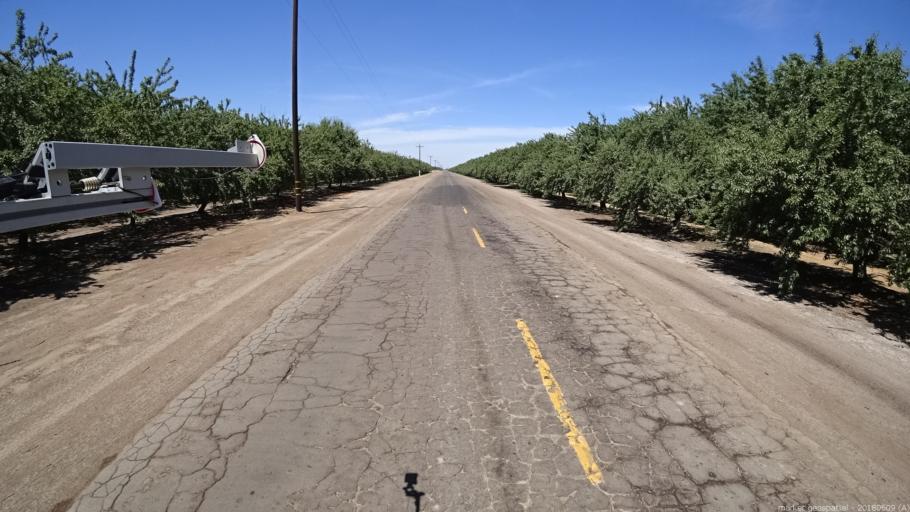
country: US
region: California
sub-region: Madera County
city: Fairmead
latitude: 36.9382
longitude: -120.2258
